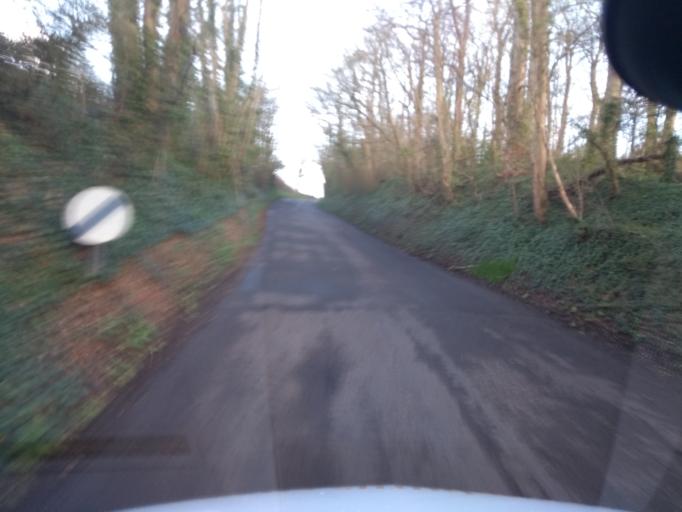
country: GB
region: England
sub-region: Somerset
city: Wedmore
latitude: 51.2291
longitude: -2.8138
